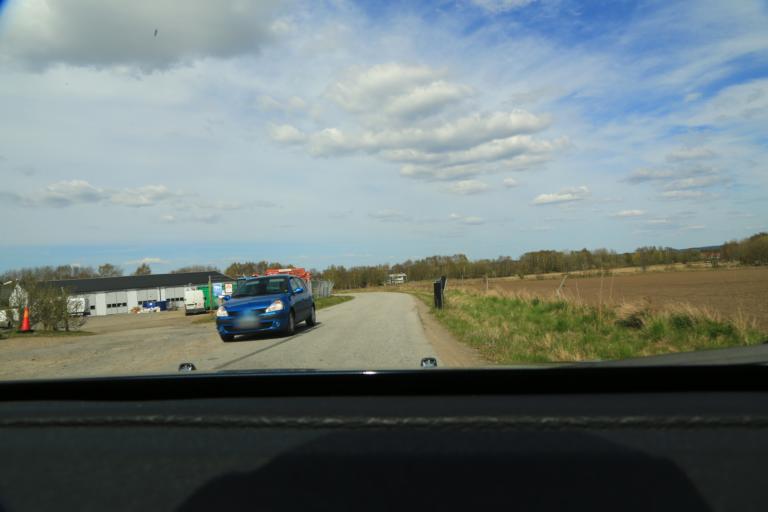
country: SE
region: Halland
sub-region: Varbergs Kommun
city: Traslovslage
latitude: 57.1122
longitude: 12.3080
